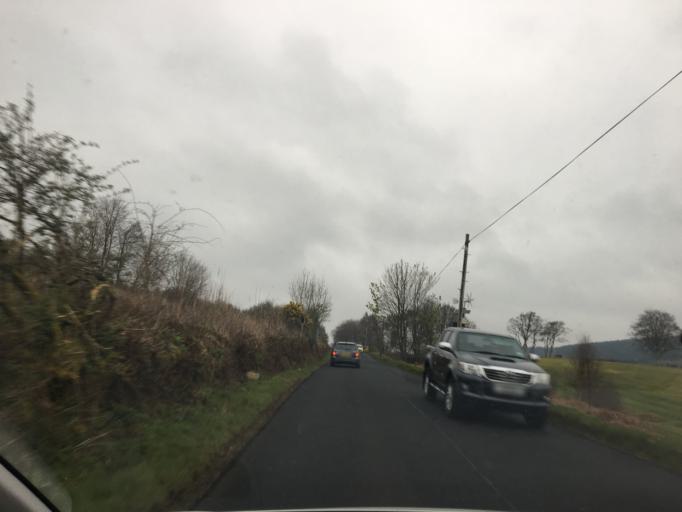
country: GB
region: Scotland
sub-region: North Ayrshire
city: Lamlash
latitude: 55.5425
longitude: -5.1292
